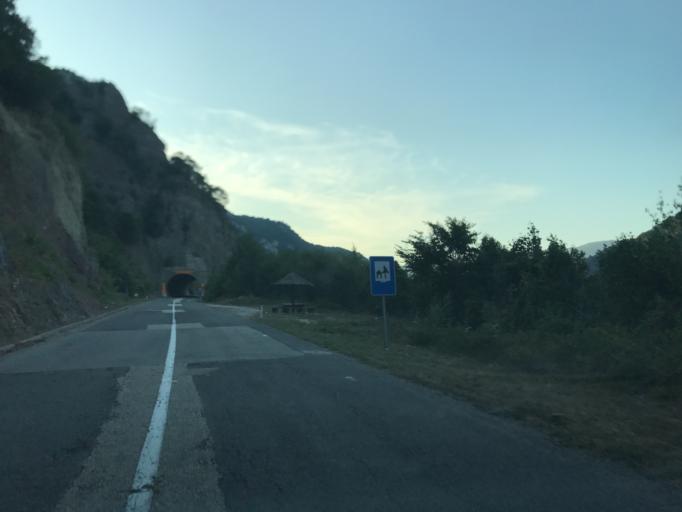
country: RO
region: Caras-Severin
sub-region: Comuna Berzasca
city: Berzasca
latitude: 44.6007
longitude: 22.0083
